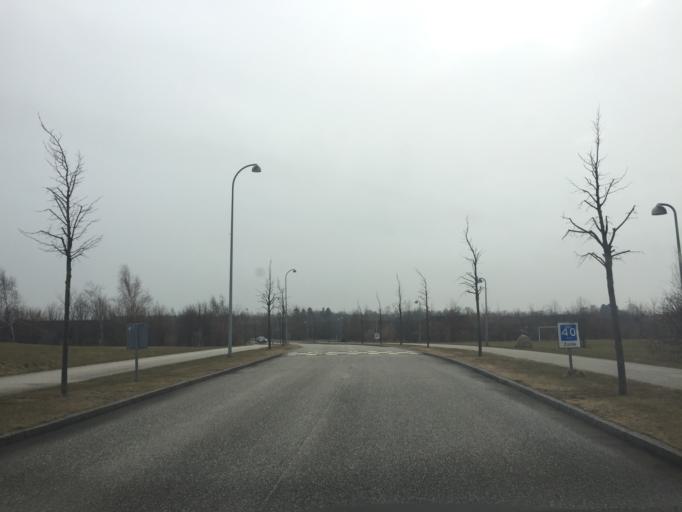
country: DK
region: Capital Region
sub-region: Hoje-Taastrup Kommune
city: Taastrup
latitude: 55.6505
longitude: 12.2455
